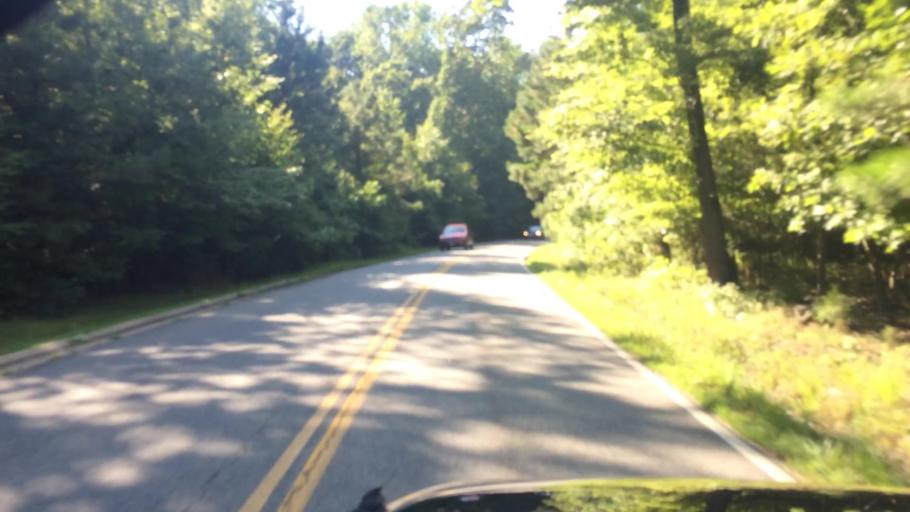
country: US
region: Virginia
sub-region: James City County
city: Williamsburg
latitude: 37.2429
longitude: -76.7939
